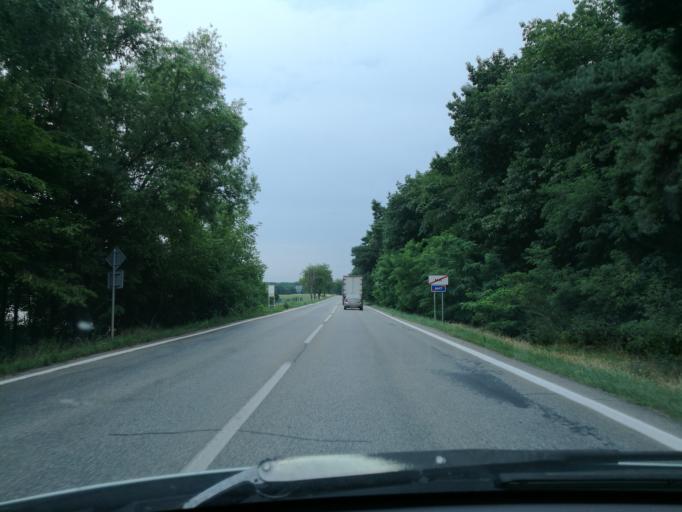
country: SK
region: Nitriansky
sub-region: Okres Komarno
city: Hurbanovo
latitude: 47.9197
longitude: 18.2092
